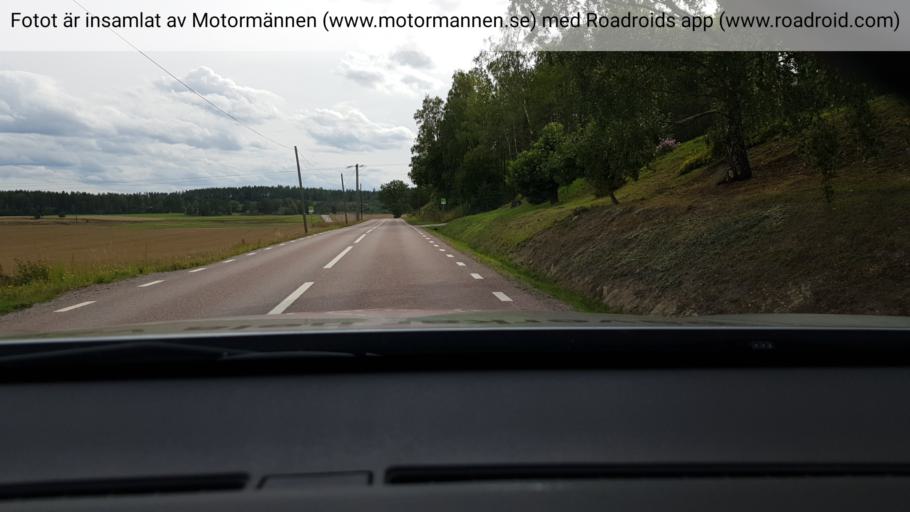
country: SE
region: Soedermanland
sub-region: Gnesta Kommun
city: Gnesta
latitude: 59.0555
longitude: 17.1588
